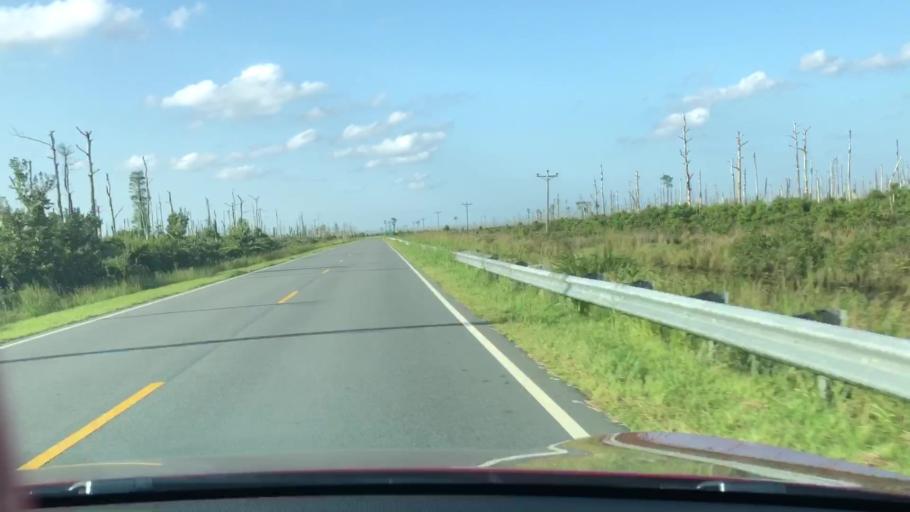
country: US
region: North Carolina
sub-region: Dare County
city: Wanchese
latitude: 35.6384
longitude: -75.7788
